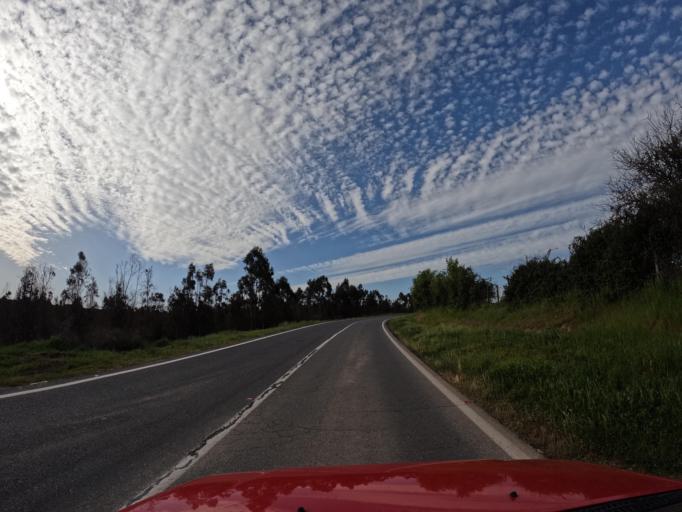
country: CL
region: O'Higgins
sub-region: Provincia de Colchagua
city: Santa Cruz
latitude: -34.2363
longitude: -71.7290
